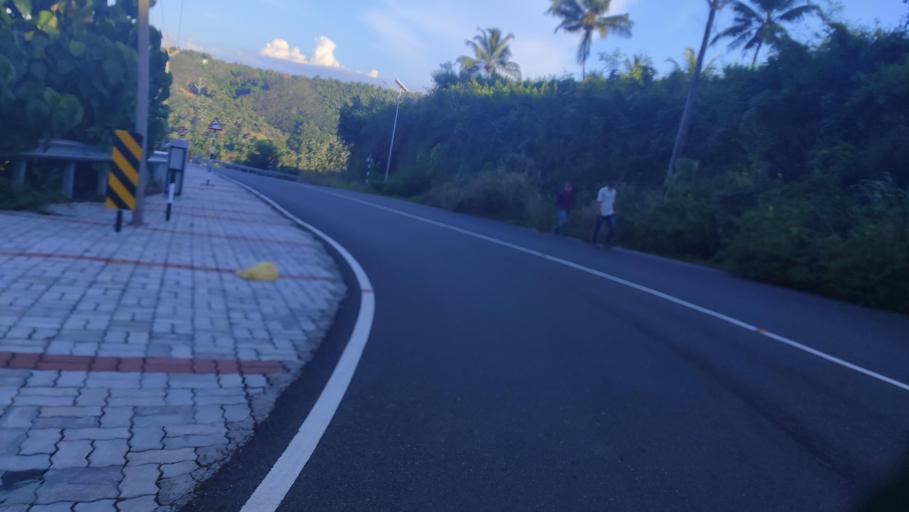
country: IN
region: Kerala
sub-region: Kasaragod District
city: Kasaragod
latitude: 12.4651
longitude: 75.0856
